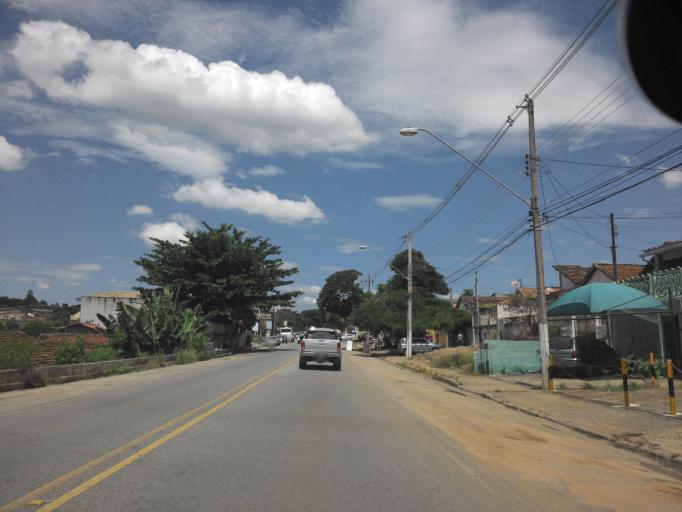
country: BR
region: Sao Paulo
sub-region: Taubate
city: Taubate
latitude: -23.0485
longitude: -45.5551
